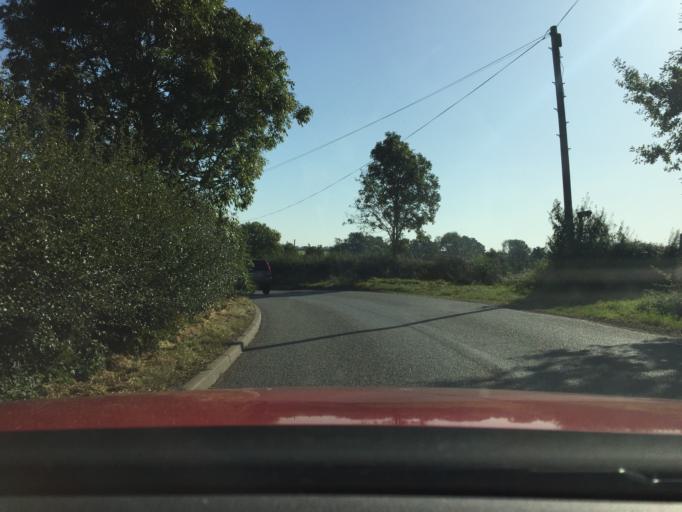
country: GB
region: England
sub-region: Leicestershire
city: Queniborough
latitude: 52.6679
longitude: -1.0237
